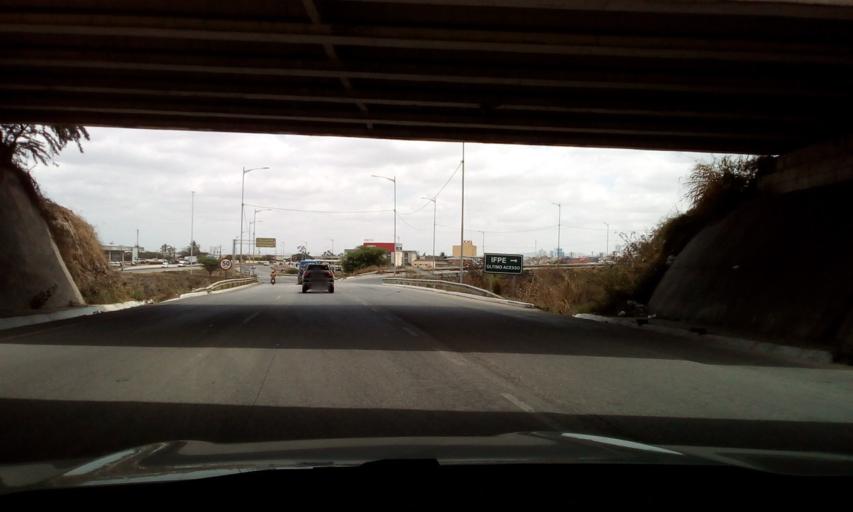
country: BR
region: Pernambuco
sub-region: Caruaru
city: Caruaru
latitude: -8.3004
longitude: -35.9881
